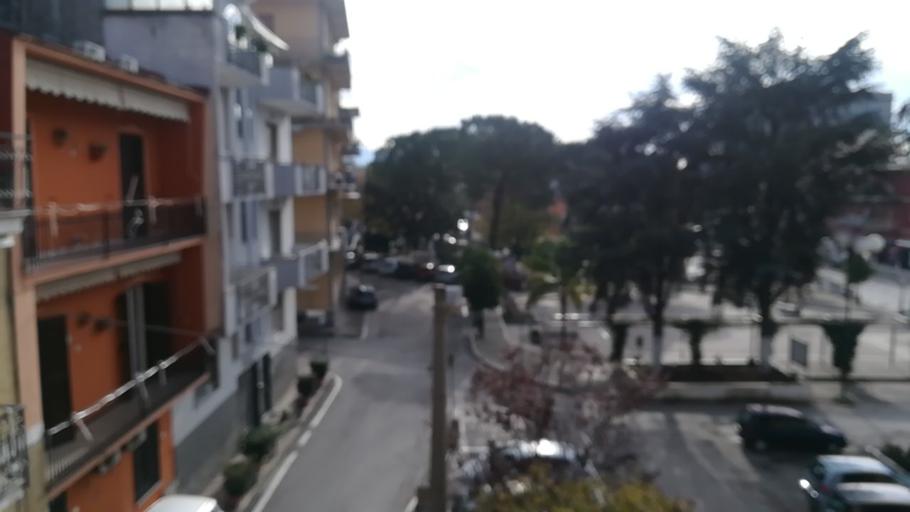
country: IT
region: Campania
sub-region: Provincia di Caserta
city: Montedecoro
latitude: 40.9944
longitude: 14.4213
